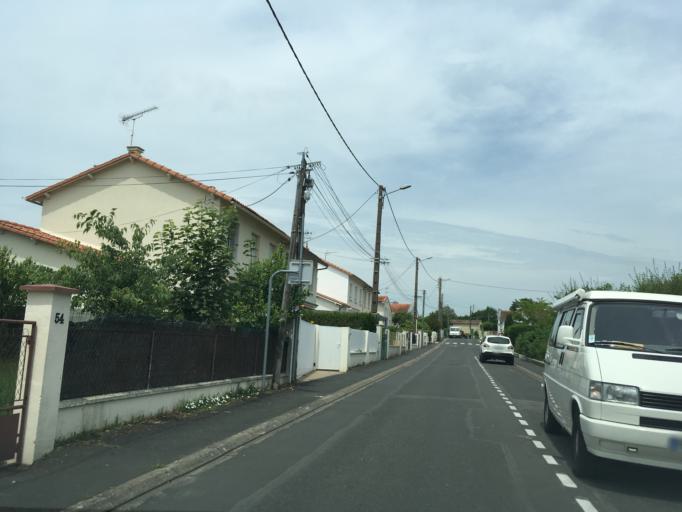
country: FR
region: Poitou-Charentes
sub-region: Departement des Deux-Sevres
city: Niort
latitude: 46.3211
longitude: -0.4855
